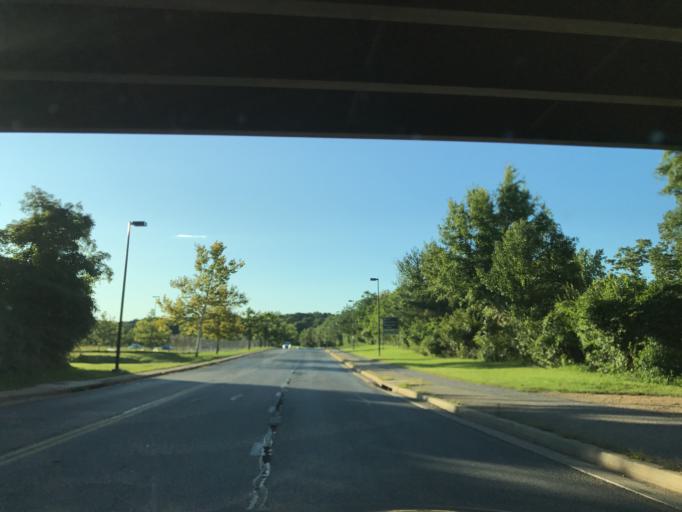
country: US
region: Maryland
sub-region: Prince George's County
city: Berwyn Heights
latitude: 39.0113
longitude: -76.9042
